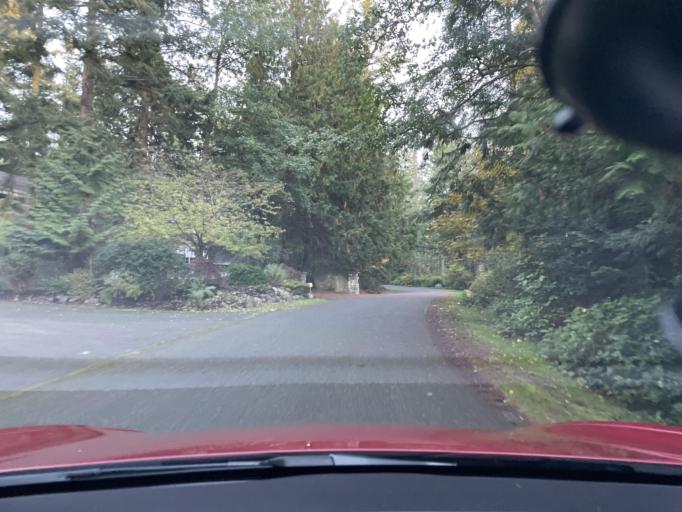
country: US
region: Washington
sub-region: San Juan County
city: Friday Harbor
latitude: 48.6199
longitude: -123.1492
